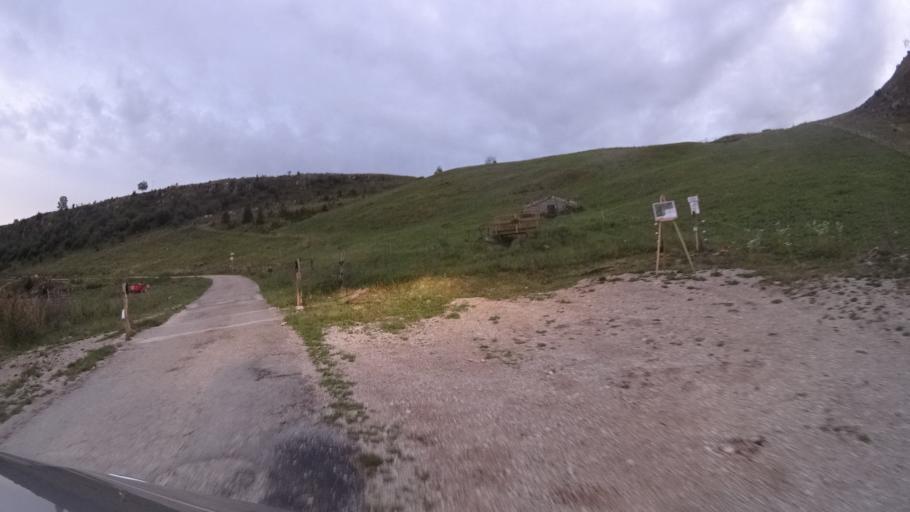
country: CH
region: Vaud
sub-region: Jura-Nord vaudois District
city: Le Chenit
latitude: 46.6716
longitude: 6.1151
